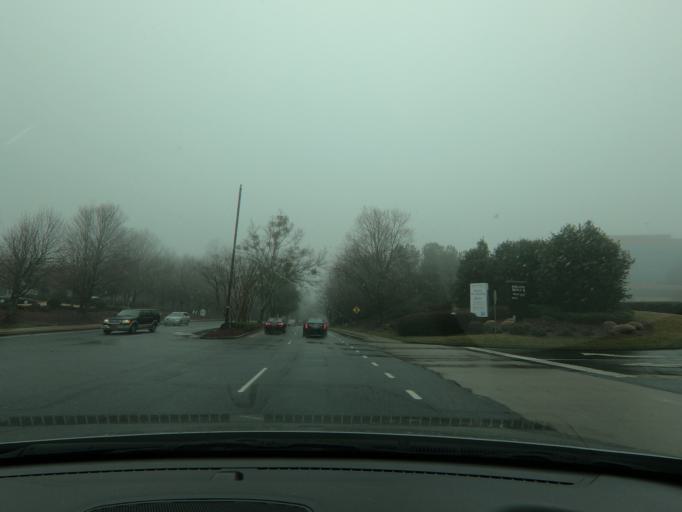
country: US
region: Georgia
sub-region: Fulton County
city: Alpharetta
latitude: 34.0745
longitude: -84.2588
